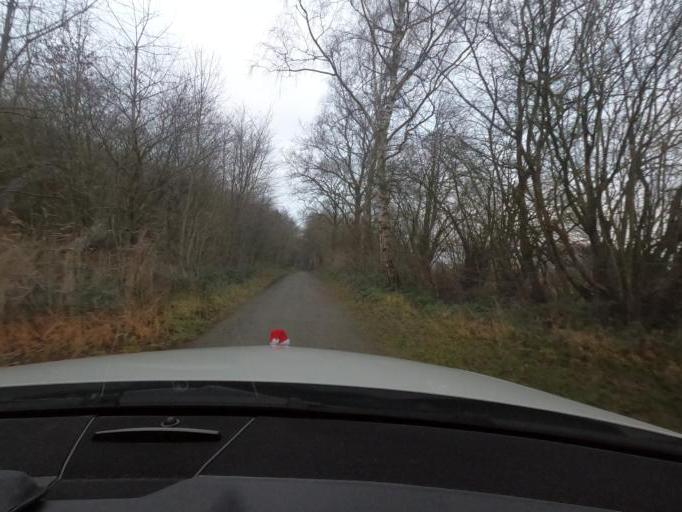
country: DK
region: South Denmark
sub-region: Sonderborg Kommune
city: Sonderborg
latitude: 54.8966
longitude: 9.8511
